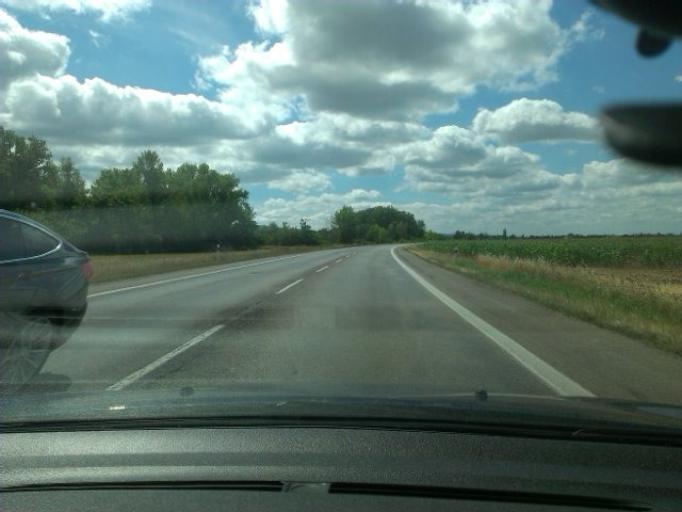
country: SK
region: Trnavsky
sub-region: Okres Trnava
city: Piestany
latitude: 48.6331
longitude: 17.8393
